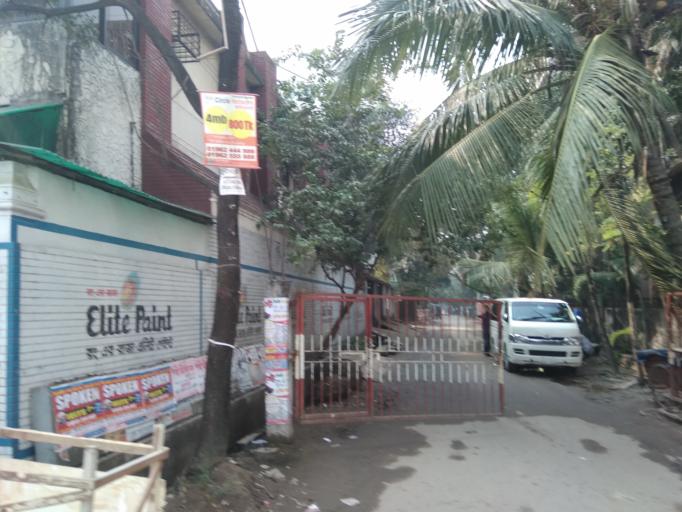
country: BD
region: Dhaka
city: Tungi
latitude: 23.8705
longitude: 90.3998
